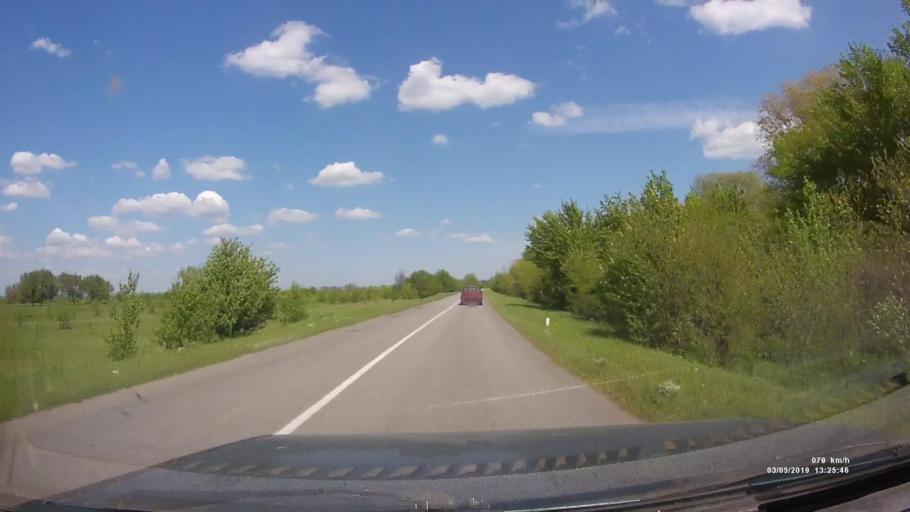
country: RU
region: Rostov
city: Semikarakorsk
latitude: 47.5689
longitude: 40.8084
